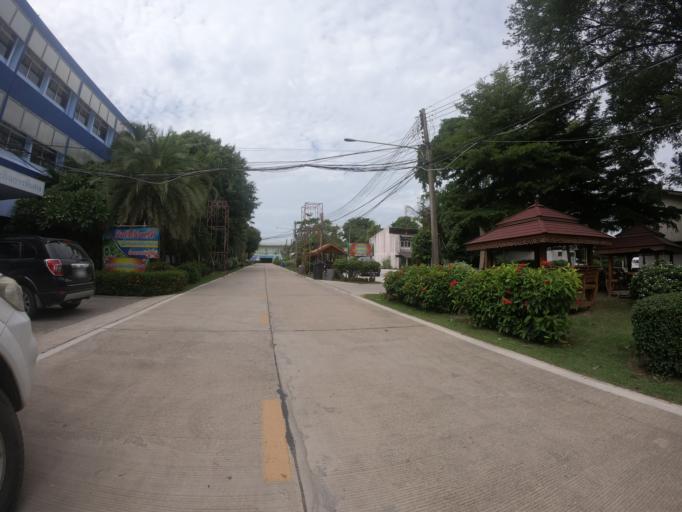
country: TH
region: Pathum Thani
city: Nong Suea
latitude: 14.0730
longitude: 100.8870
